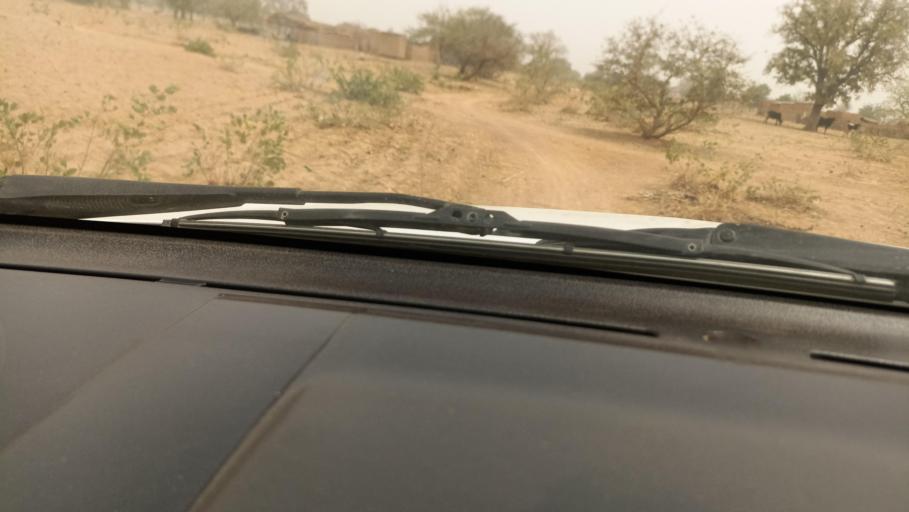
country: BF
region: Boucle du Mouhoun
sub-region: Province du Nayala
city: Toma
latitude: 12.8554
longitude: -2.7983
